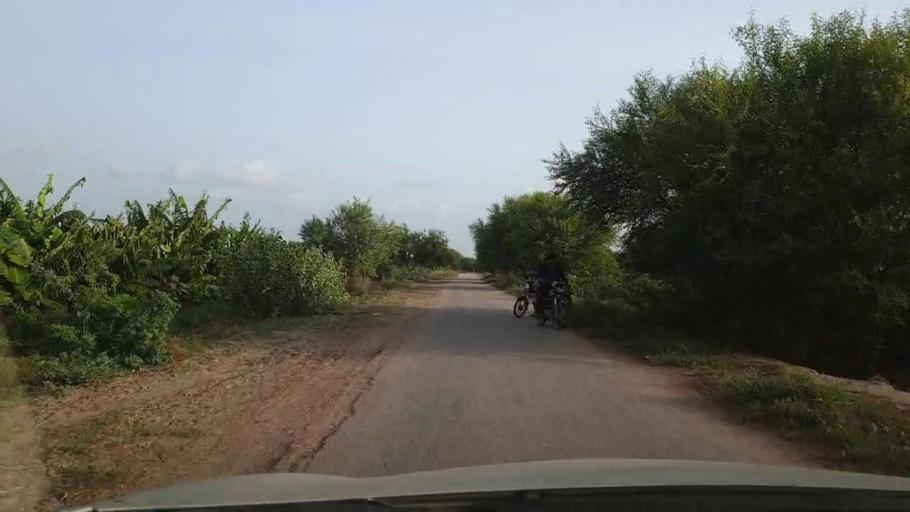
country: PK
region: Sindh
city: Tando Ghulam Ali
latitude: 25.1005
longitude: 68.8849
